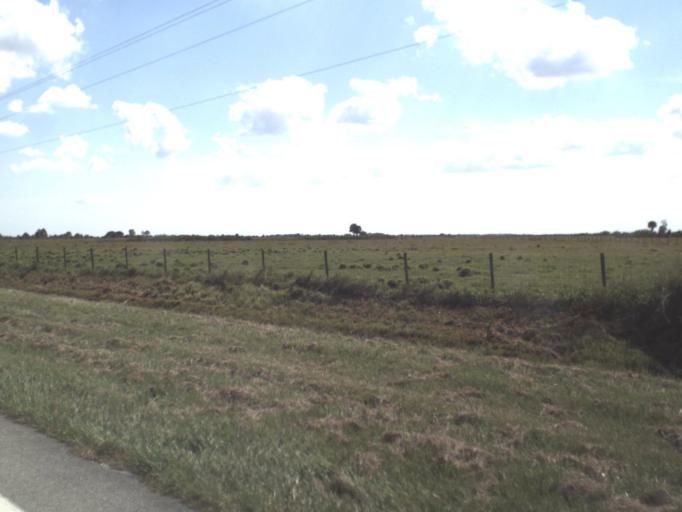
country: US
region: Florida
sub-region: Okeechobee County
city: Okeechobee
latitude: 27.3733
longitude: -80.9807
